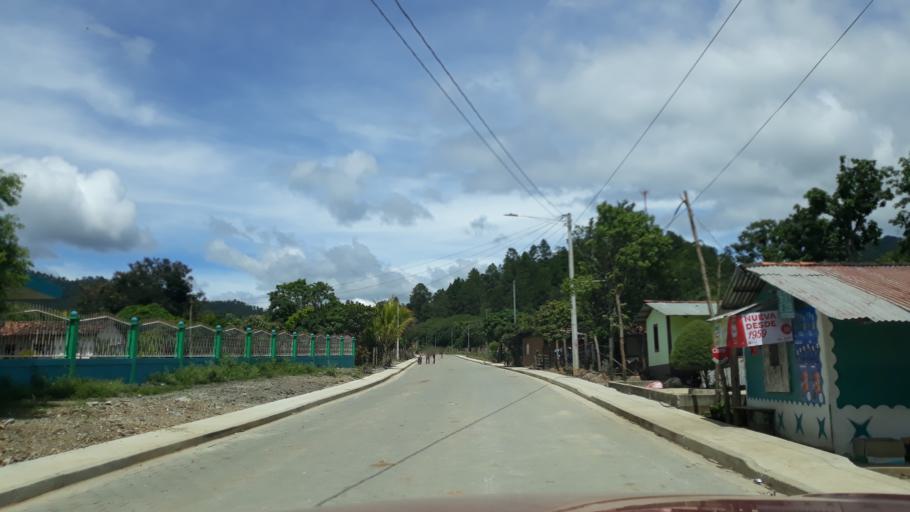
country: HN
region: El Paraiso
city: Santa Cruz
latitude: 13.7343
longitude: -86.6242
